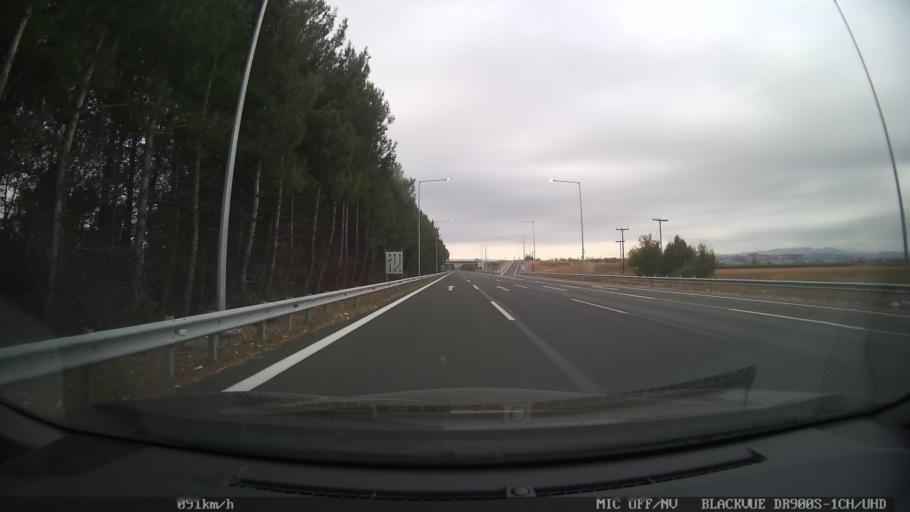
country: GR
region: Central Macedonia
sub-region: Nomos Pierias
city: Aiginio
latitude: 40.5136
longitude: 22.5703
